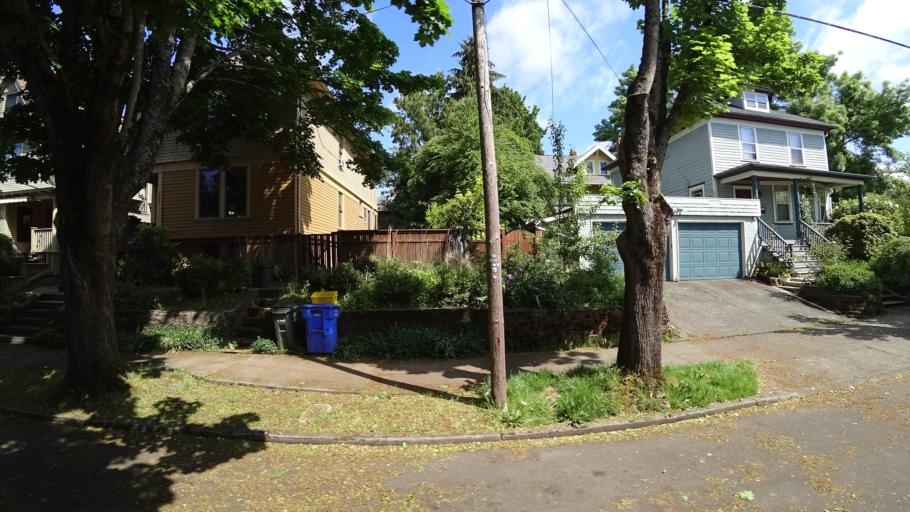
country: US
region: Oregon
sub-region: Multnomah County
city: Portland
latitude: 45.5143
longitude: -122.6449
